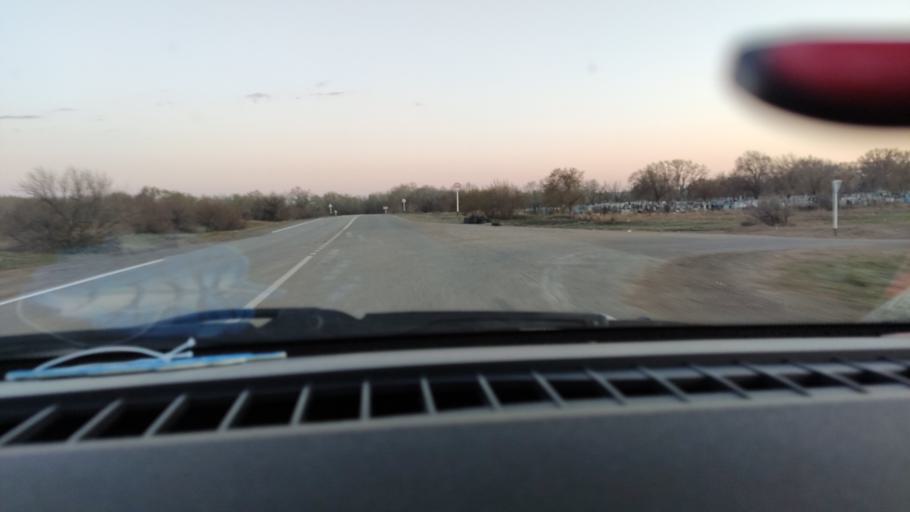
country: RU
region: Saratov
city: Privolzhskiy
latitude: 51.1902
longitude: 45.9151
